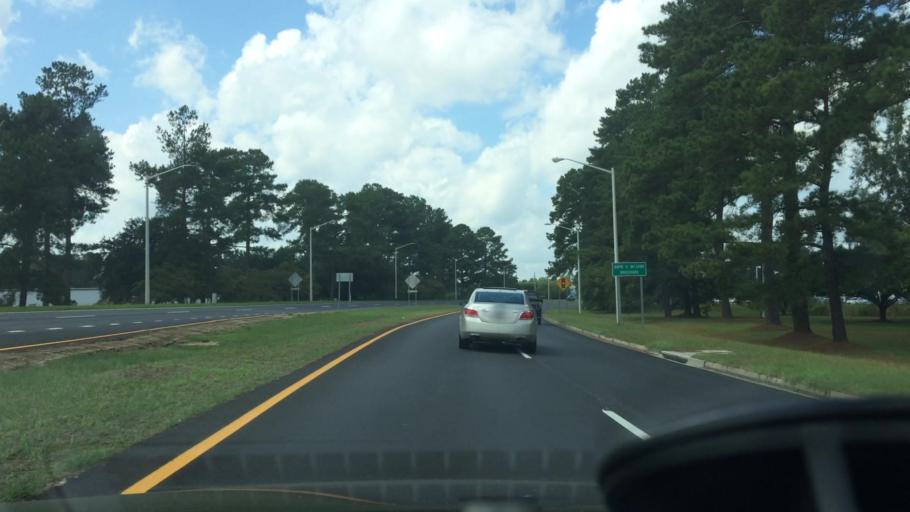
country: US
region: South Carolina
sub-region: Florence County
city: Florence
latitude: 34.1876
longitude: -79.8133
